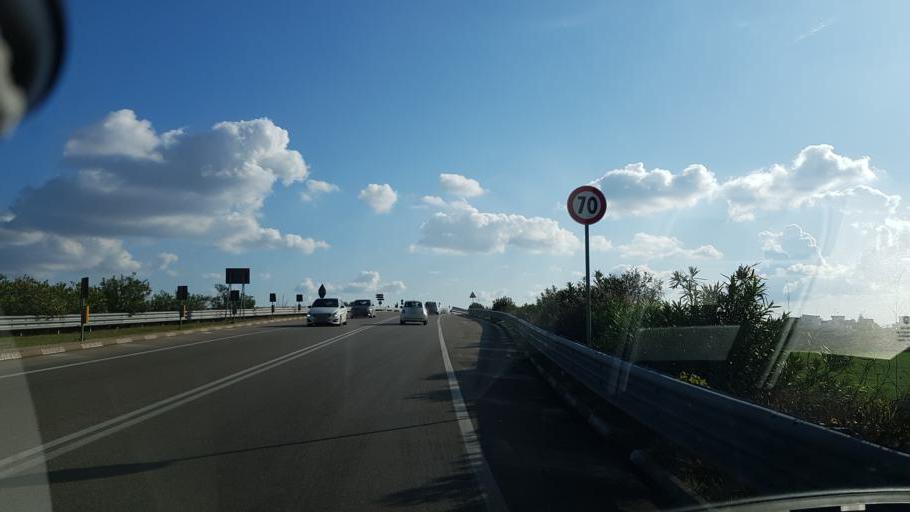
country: IT
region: Apulia
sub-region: Provincia di Lecce
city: Salice Salentino
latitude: 40.3903
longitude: 17.9684
